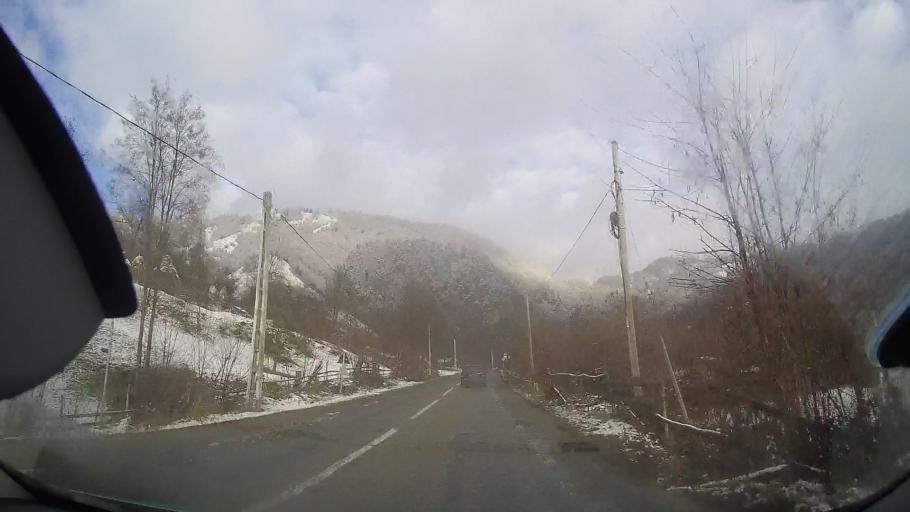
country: RO
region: Alba
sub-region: Oras Baia de Aries
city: Baia de Aries
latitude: 46.3968
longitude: 23.3002
